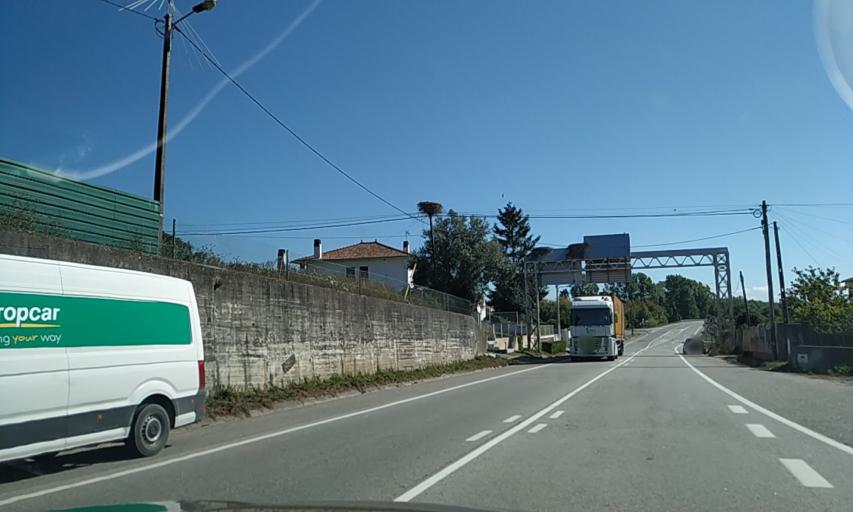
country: PT
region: Aveiro
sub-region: Estarreja
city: Salreu
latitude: 40.6887
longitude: -8.5567
